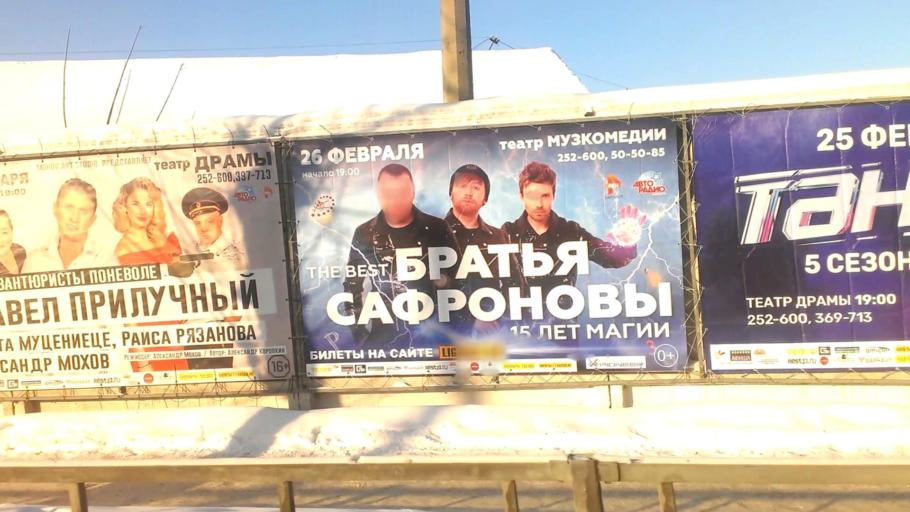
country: RU
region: Altai Krai
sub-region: Gorod Barnaulskiy
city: Barnaul
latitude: 53.3422
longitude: 83.7481
